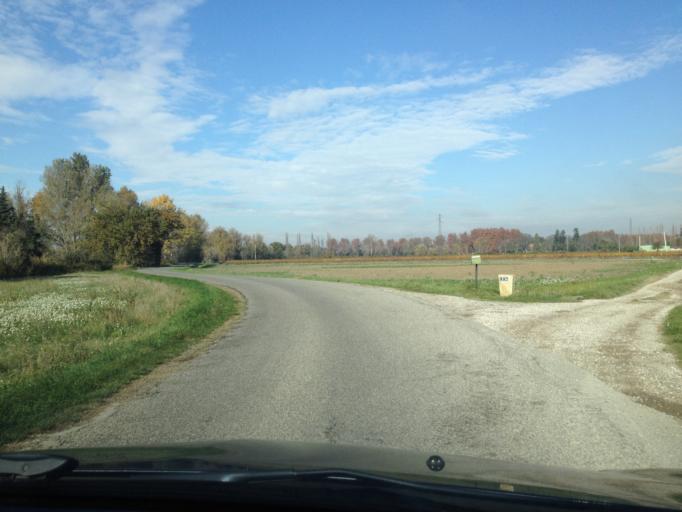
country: FR
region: Provence-Alpes-Cote d'Azur
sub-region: Departement du Vaucluse
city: Bedarrides
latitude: 44.0543
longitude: 4.8987
